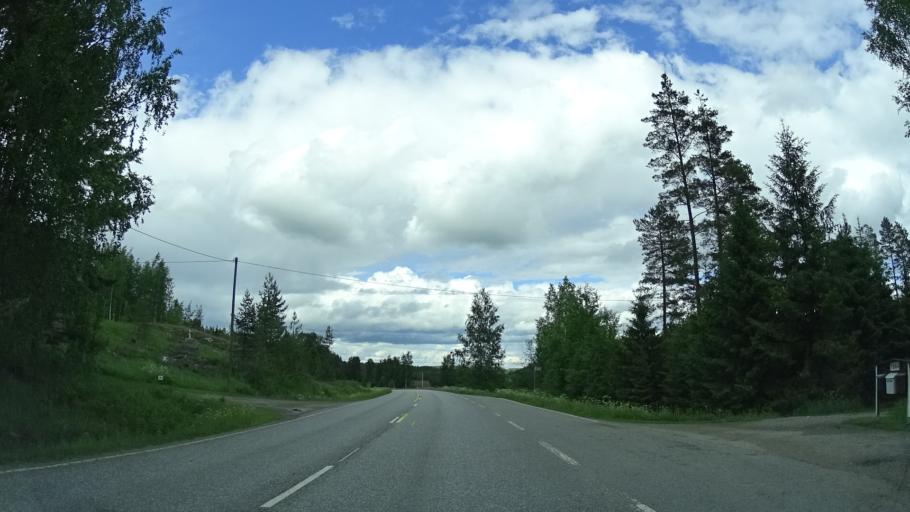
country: FI
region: Paijanne Tavastia
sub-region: Lahti
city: Sysmae
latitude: 61.3690
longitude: 25.6385
